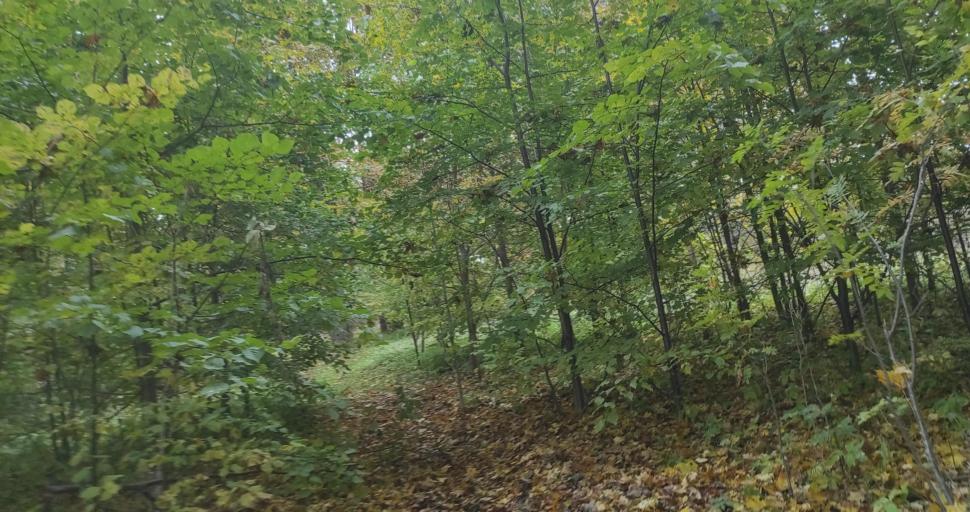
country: LV
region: Kandava
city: Kandava
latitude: 57.0158
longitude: 22.7577
